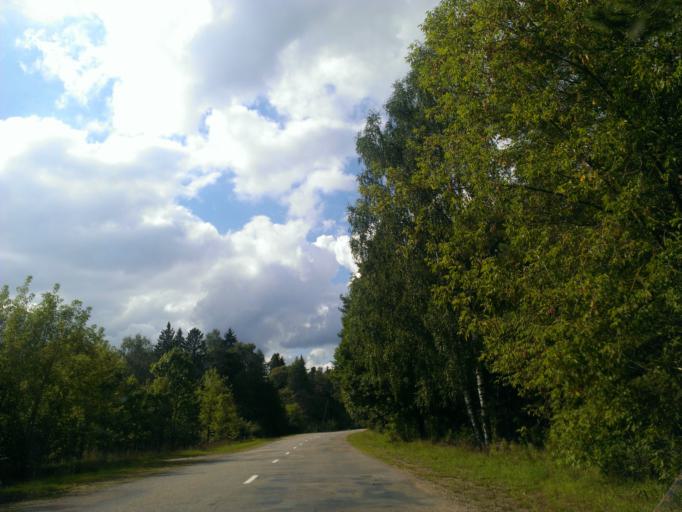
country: LV
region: Garkalne
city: Garkalne
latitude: 56.9660
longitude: 24.4963
